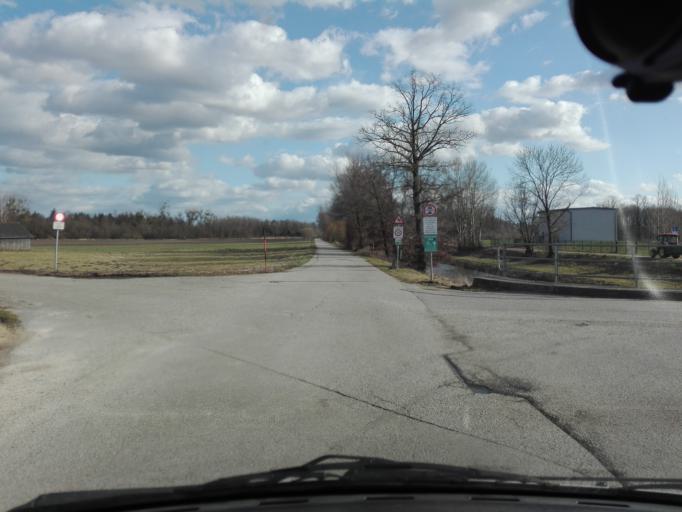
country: AT
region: Upper Austria
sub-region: Politischer Bezirk Perg
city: Perg
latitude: 48.2320
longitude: 14.6477
